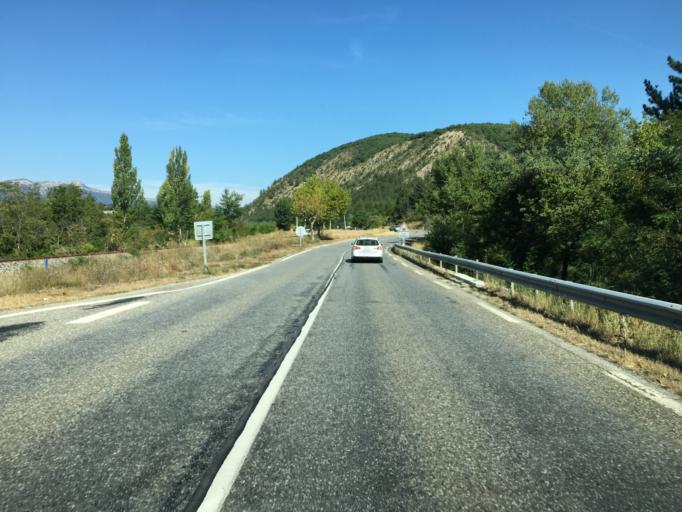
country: FR
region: Provence-Alpes-Cote d'Azur
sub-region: Departement des Hautes-Alpes
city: Laragne-Monteglin
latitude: 44.3311
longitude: 5.7891
